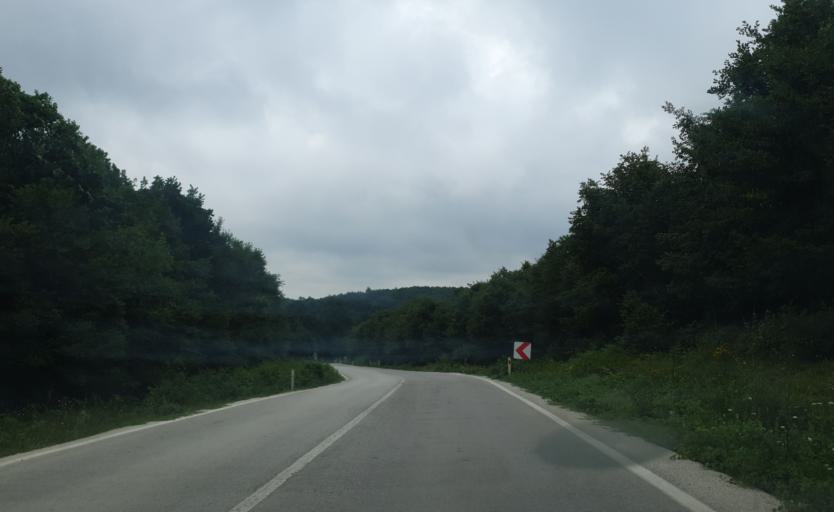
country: TR
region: Kirklareli
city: Salmydessus
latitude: 41.5828
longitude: 28.0714
